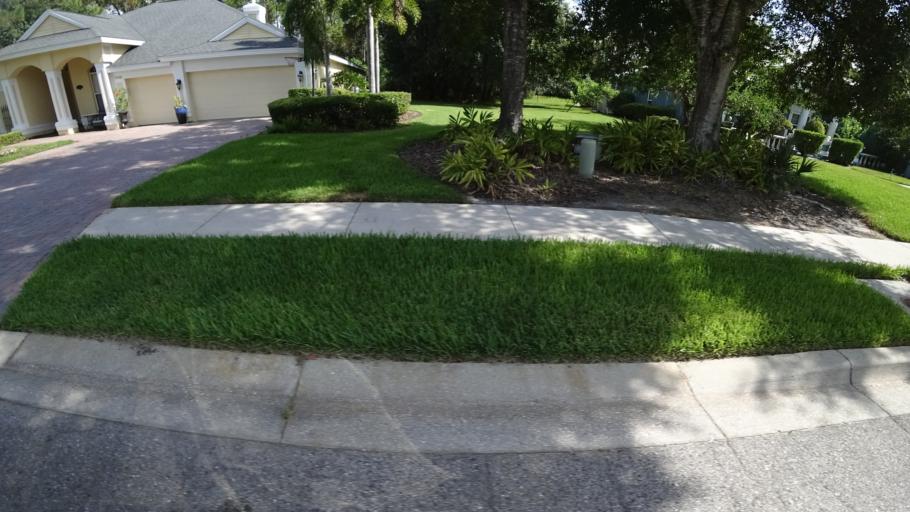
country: US
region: Florida
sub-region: Sarasota County
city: The Meadows
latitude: 27.4050
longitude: -82.4337
